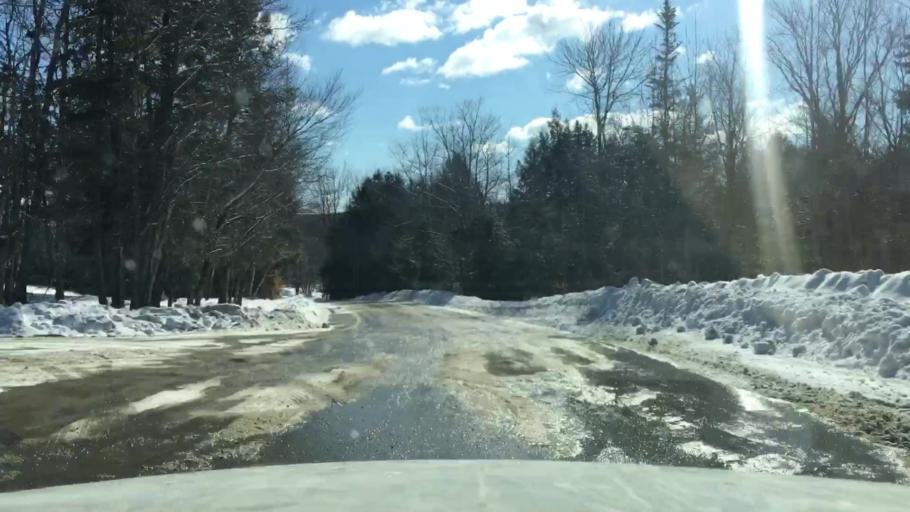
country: US
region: Maine
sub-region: Washington County
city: Calais
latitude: 45.0710
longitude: -67.4991
